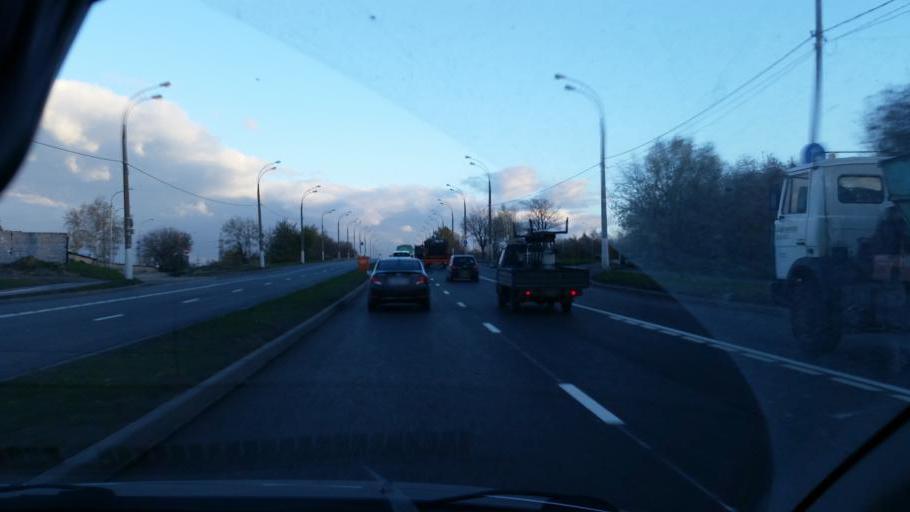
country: RU
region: Moskovskaya
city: Biryulevo Zapadnoye
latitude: 55.6062
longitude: 37.6274
